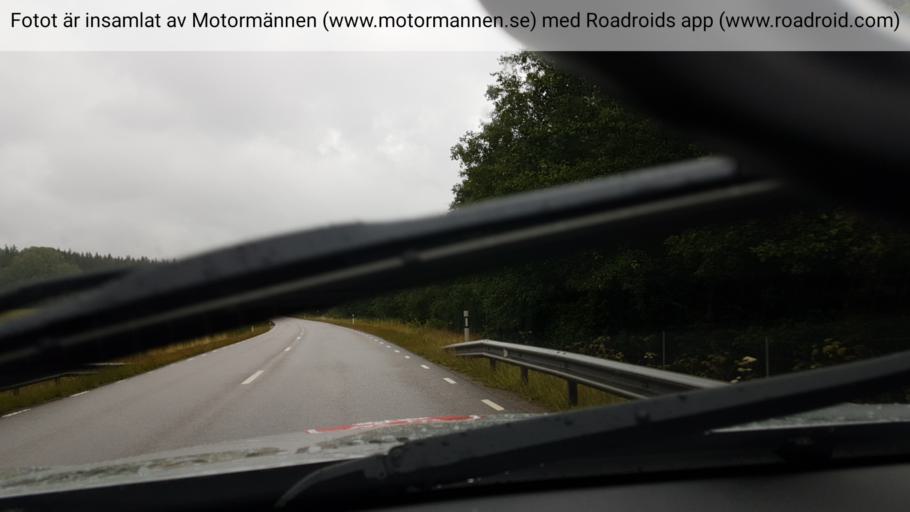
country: SE
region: Vaestra Goetaland
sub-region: Bengtsfors Kommun
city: Billingsfors
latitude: 58.9557
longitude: 12.2301
